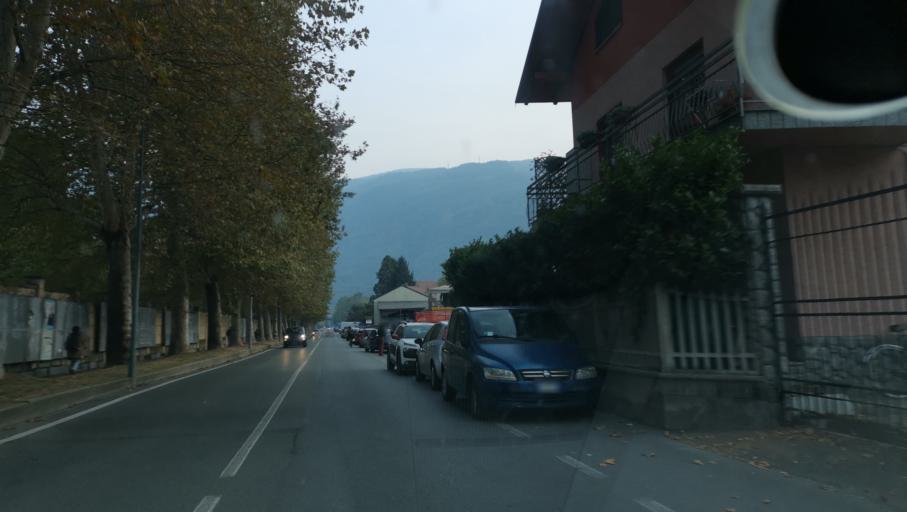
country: IT
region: Piedmont
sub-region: Provincia di Torino
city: Condove
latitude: 45.1123
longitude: 7.3137
